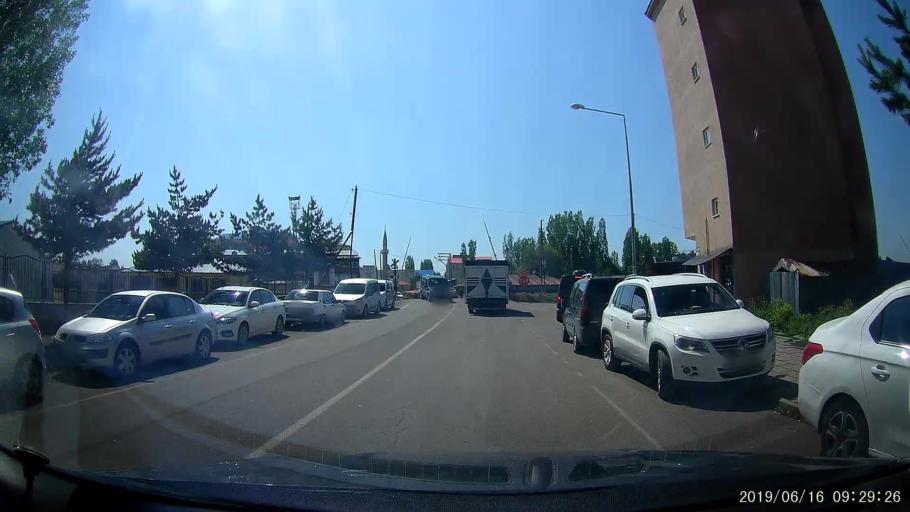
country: TR
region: Kars
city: Kars
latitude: 40.6018
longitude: 43.1039
